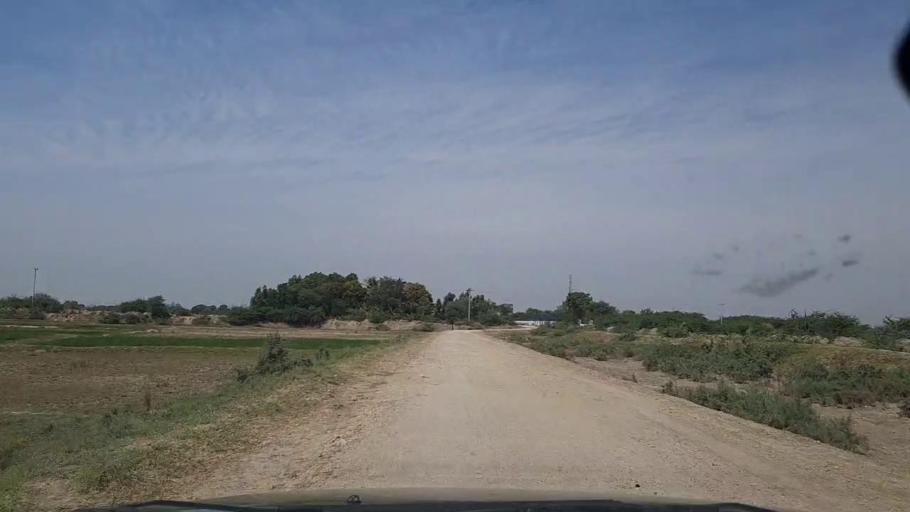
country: PK
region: Sindh
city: Mirpur Batoro
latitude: 24.6524
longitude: 68.1801
